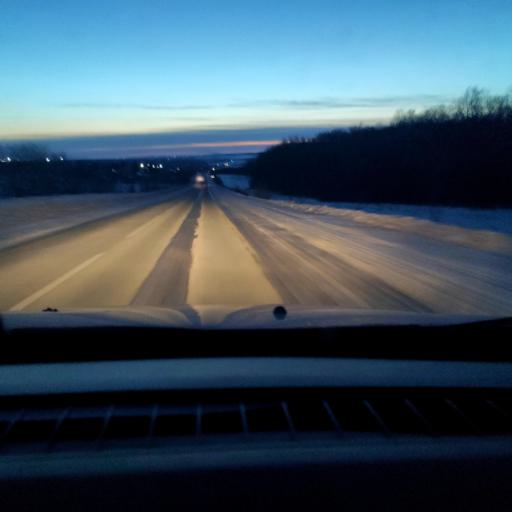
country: RU
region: Samara
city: Kinel'
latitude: 53.3020
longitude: 50.7875
